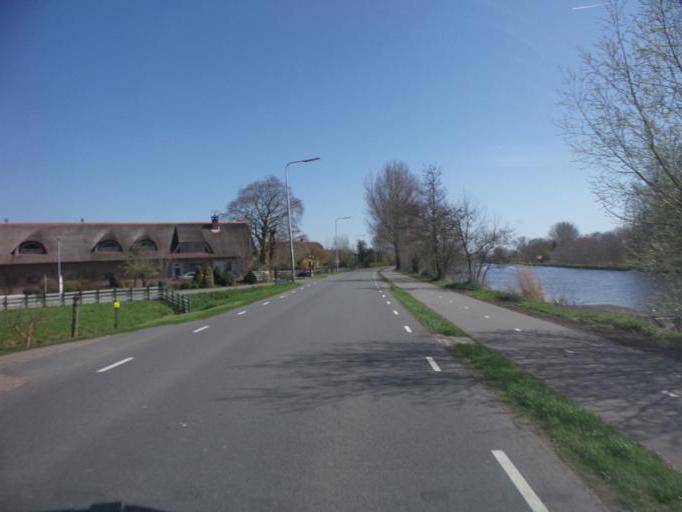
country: NL
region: South Holland
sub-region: Bodegraven-Reeuwijk
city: Bodegraven
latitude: 52.0861
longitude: 4.7966
